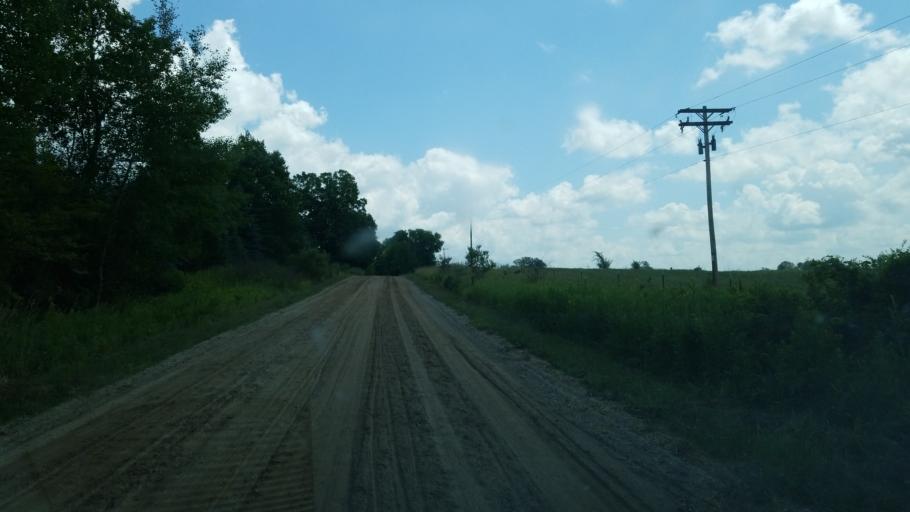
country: US
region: Michigan
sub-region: Mecosta County
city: Canadian Lakes
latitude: 43.5693
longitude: -85.3856
